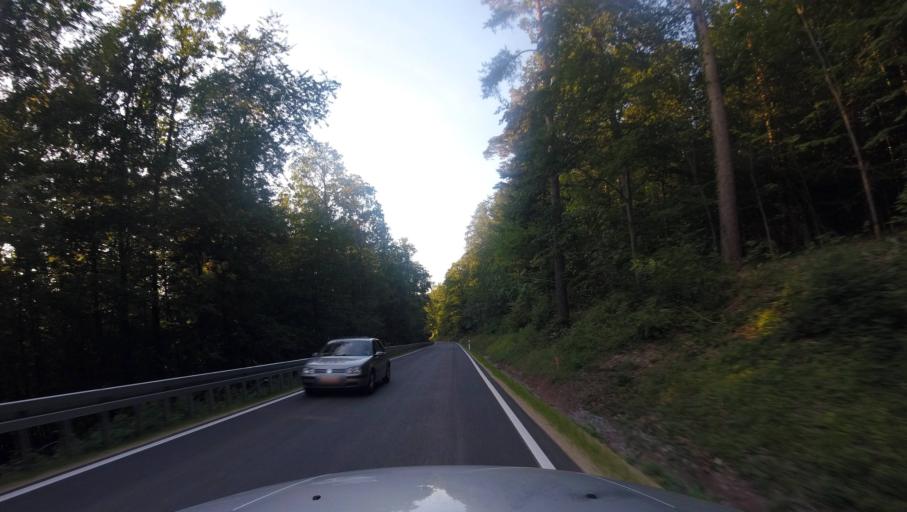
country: DE
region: Baden-Wuerttemberg
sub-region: Regierungsbezirk Stuttgart
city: Rudersberg
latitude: 48.9182
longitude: 9.5349
